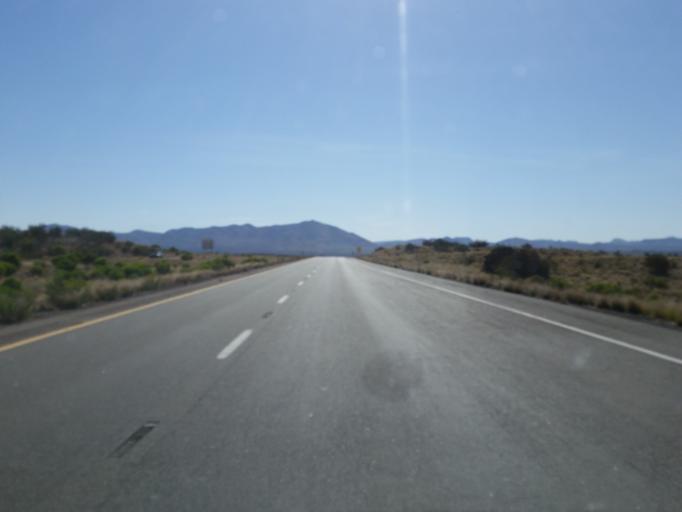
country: US
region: Arizona
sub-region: Mohave County
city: New Kingman-Butler
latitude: 35.1595
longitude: -113.6903
